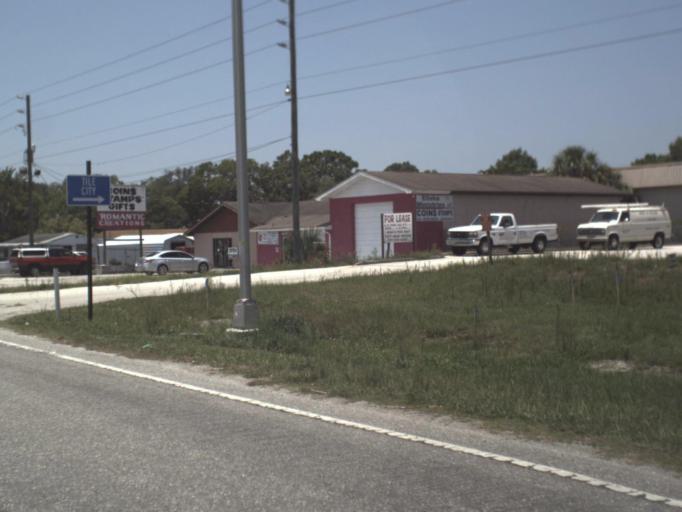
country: US
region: Florida
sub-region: Pasco County
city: Hudson
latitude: 28.3766
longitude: -82.6816
